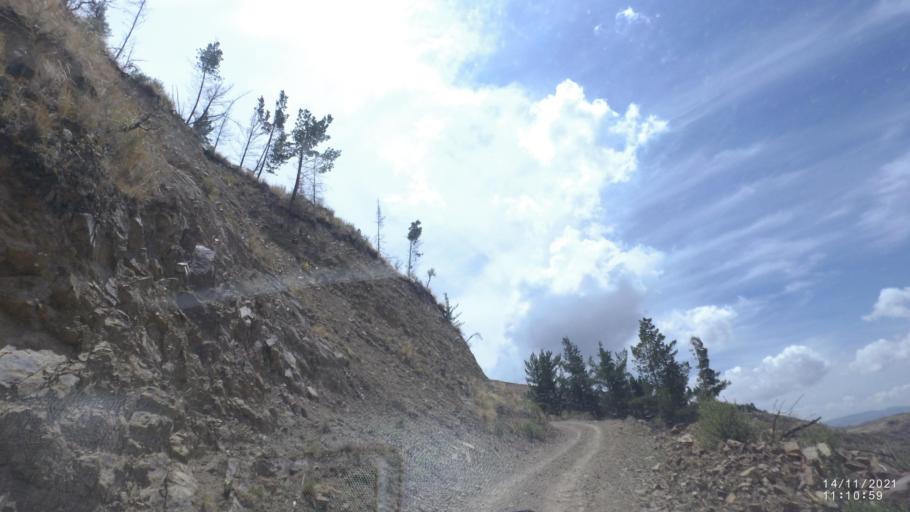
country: BO
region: Cochabamba
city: Cochabamba
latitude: -17.3283
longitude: -66.0516
